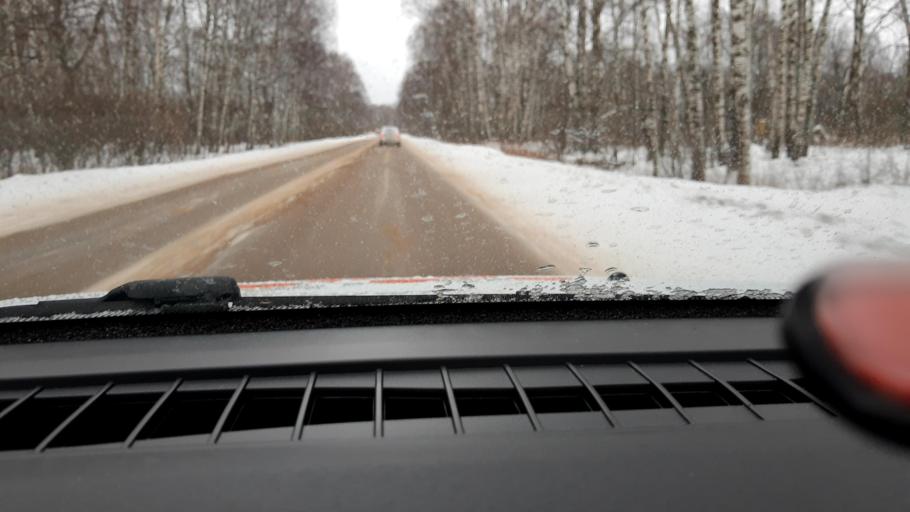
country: RU
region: Nizjnij Novgorod
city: Afonino
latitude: 56.3177
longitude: 44.1943
